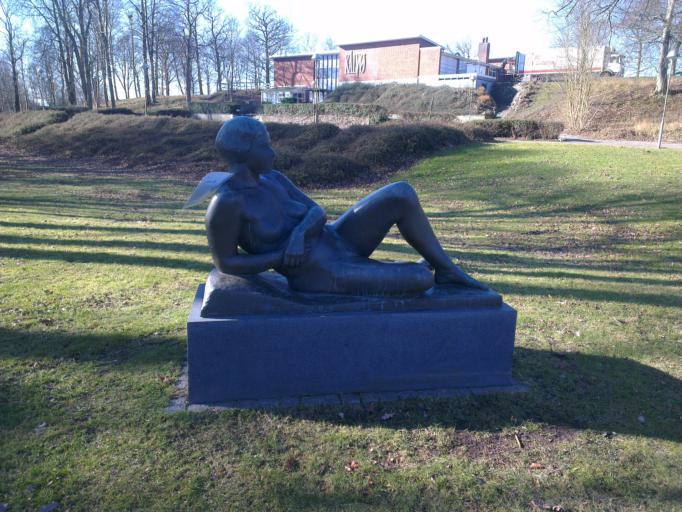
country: DK
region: Capital Region
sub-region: Frederikssund Kommune
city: Frederikssund
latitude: 55.8334
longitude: 12.0579
